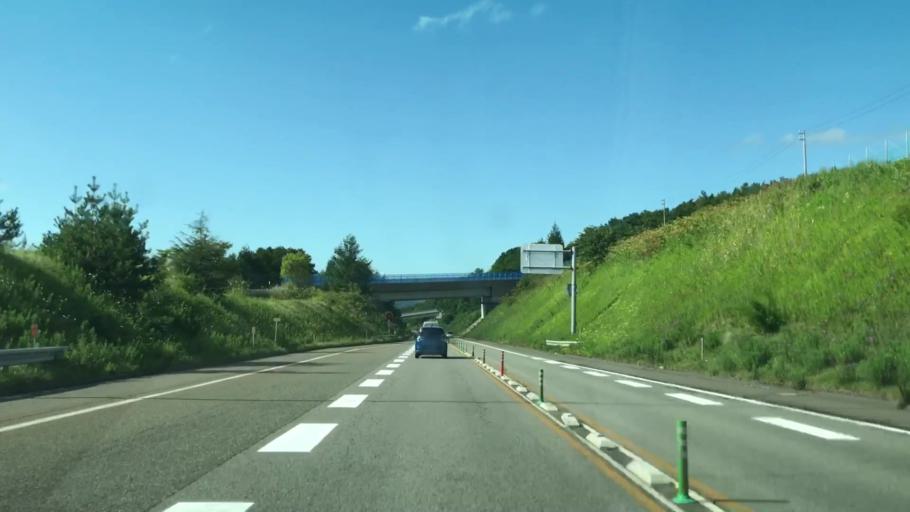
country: JP
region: Hokkaido
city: Date
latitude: 42.4690
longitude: 140.9071
